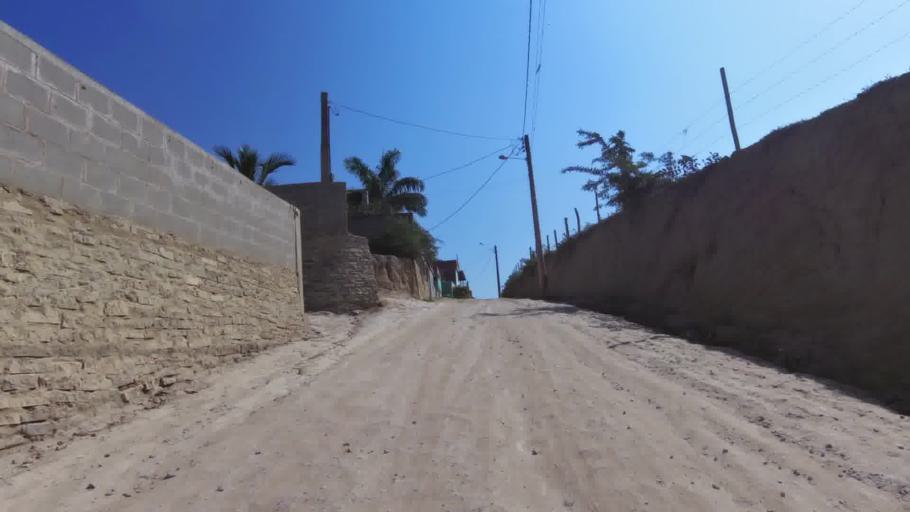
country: BR
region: Espirito Santo
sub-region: Marataizes
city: Marataizes
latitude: -21.0284
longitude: -40.8196
